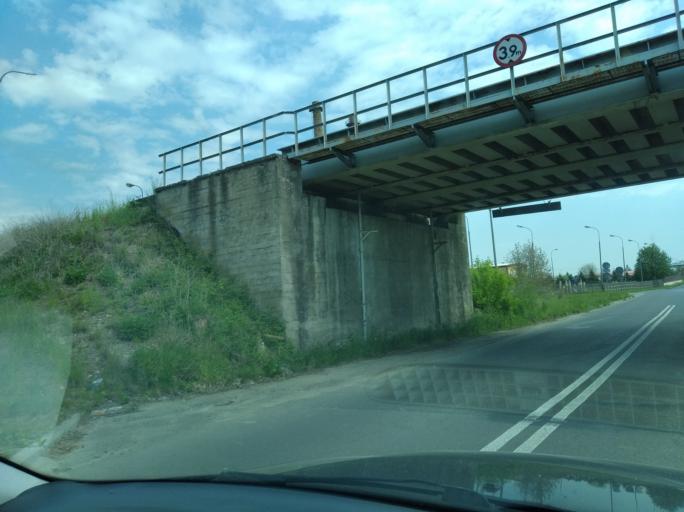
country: PL
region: Subcarpathian Voivodeship
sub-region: Powiat jaroslawski
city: Jaroslaw
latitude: 50.0006
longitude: 22.7063
